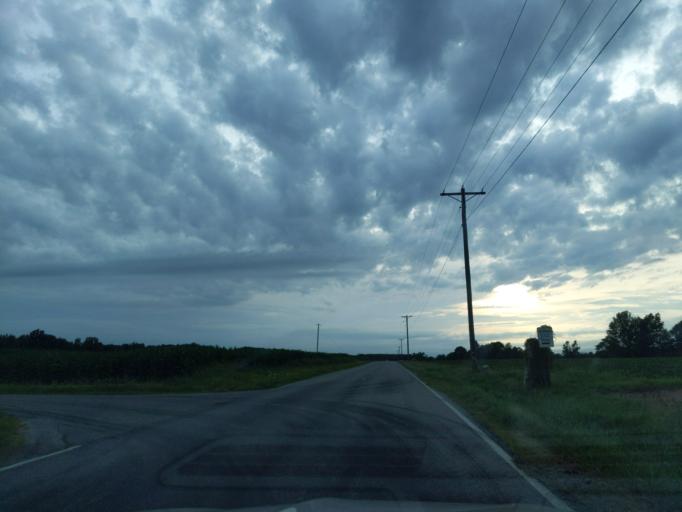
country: US
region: Indiana
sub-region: Ripley County
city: Osgood
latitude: 39.1975
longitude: -85.2897
